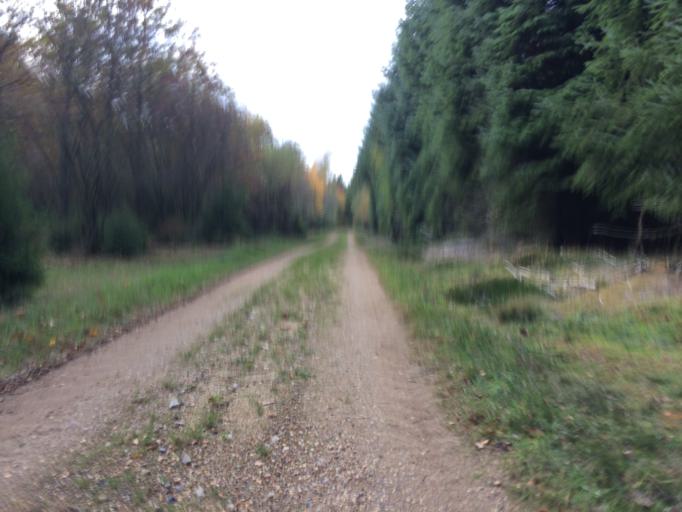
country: DK
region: Central Jutland
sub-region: Holstebro Kommune
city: Ulfborg
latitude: 56.2082
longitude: 8.4554
